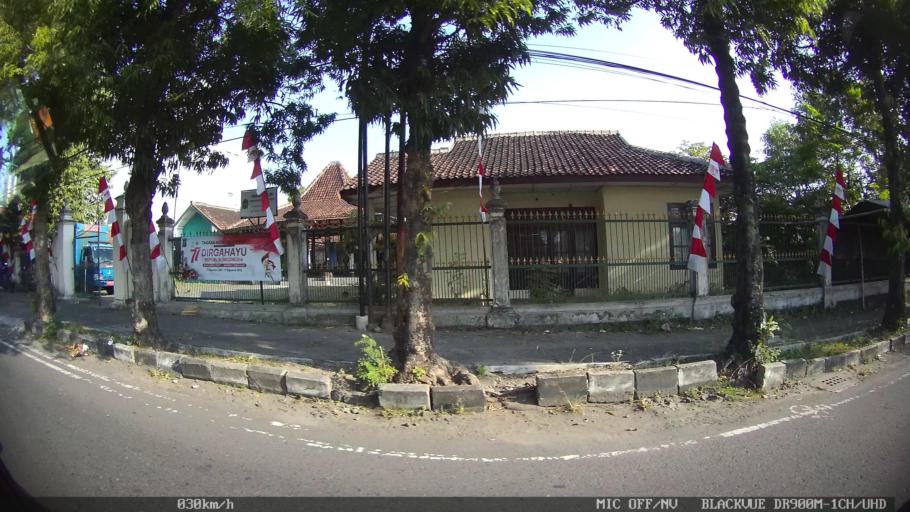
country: ID
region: Daerah Istimewa Yogyakarta
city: Yogyakarta
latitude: -7.8255
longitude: 110.3864
